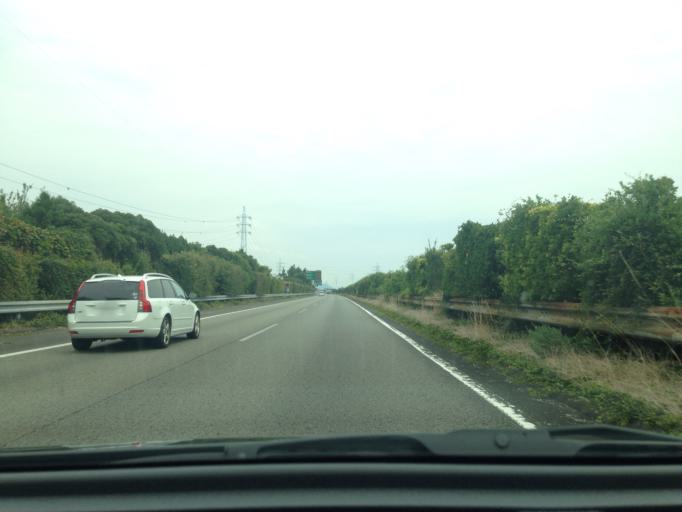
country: JP
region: Shizuoka
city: Fujieda
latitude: 34.8121
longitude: 138.2594
